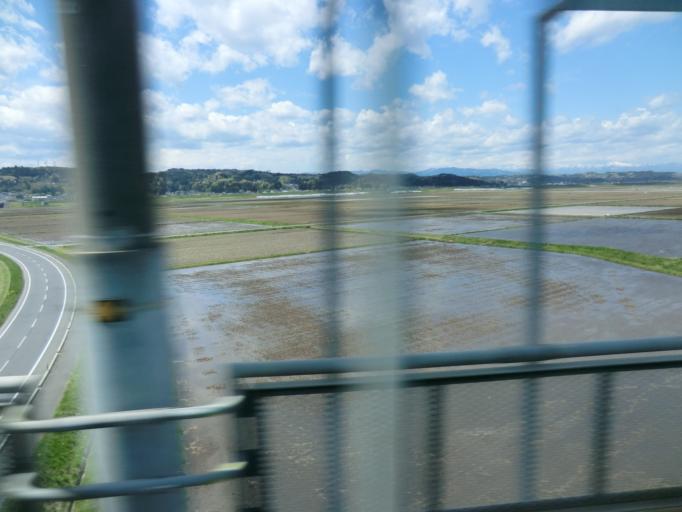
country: JP
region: Iwate
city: Ichinoseki
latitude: 38.9479
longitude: 141.1475
